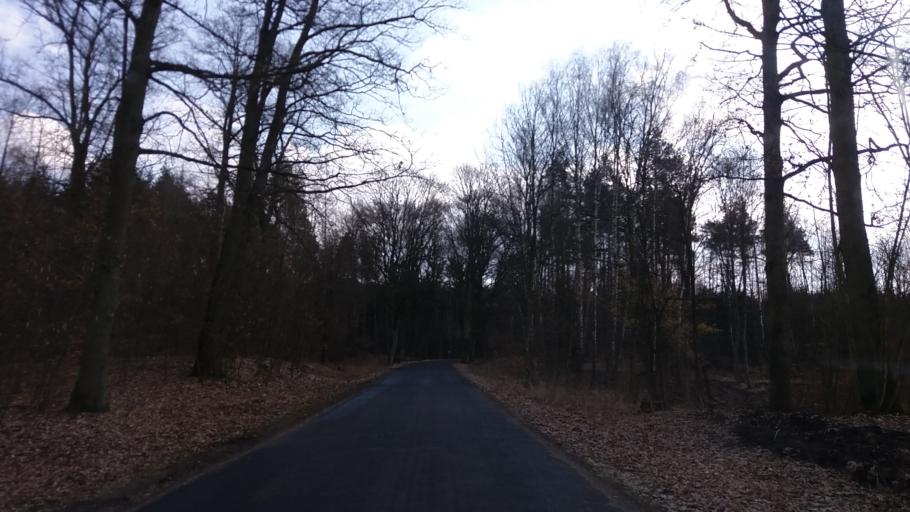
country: PL
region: West Pomeranian Voivodeship
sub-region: Powiat choszczenski
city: Recz
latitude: 53.1603
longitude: 15.6228
